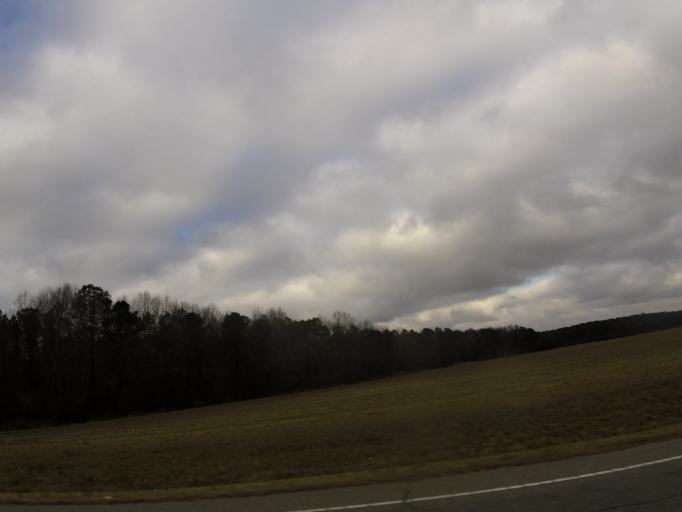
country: US
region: North Carolina
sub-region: Edgecombe County
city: Pinetops
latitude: 35.8585
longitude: -77.6947
